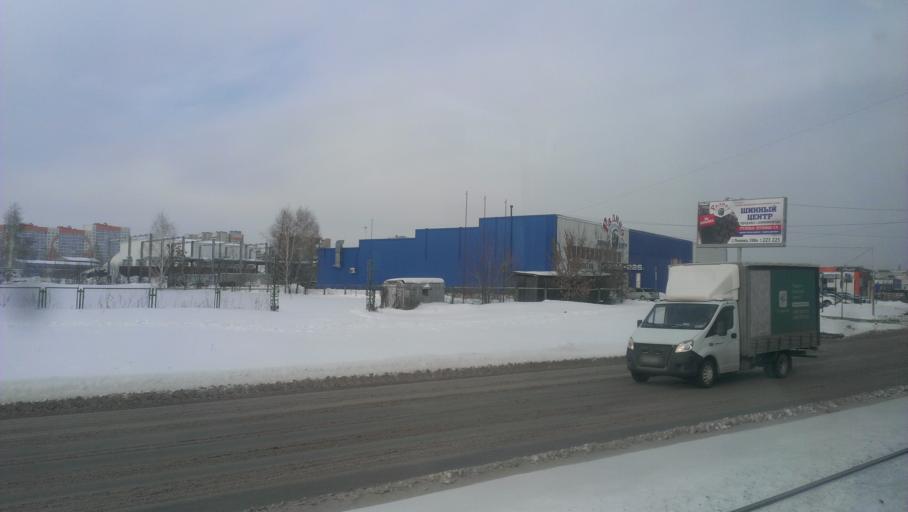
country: RU
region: Altai Krai
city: Novosilikatnyy
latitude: 53.3322
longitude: 83.6679
